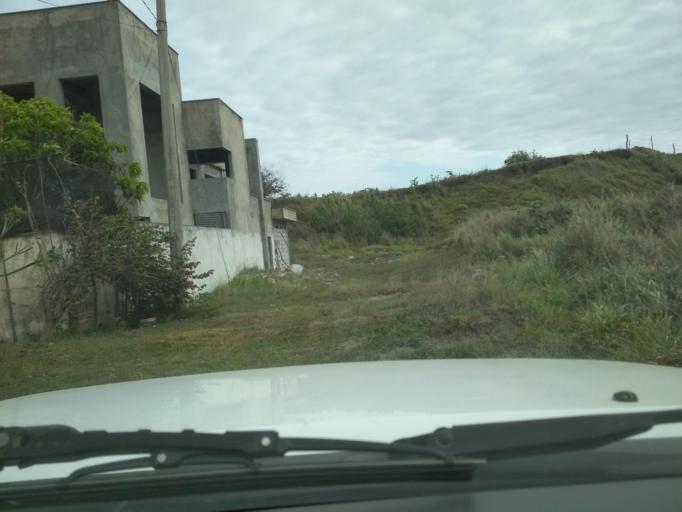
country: MX
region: Veracruz
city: Anton Lizardo
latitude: 19.0464
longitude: -95.9875
